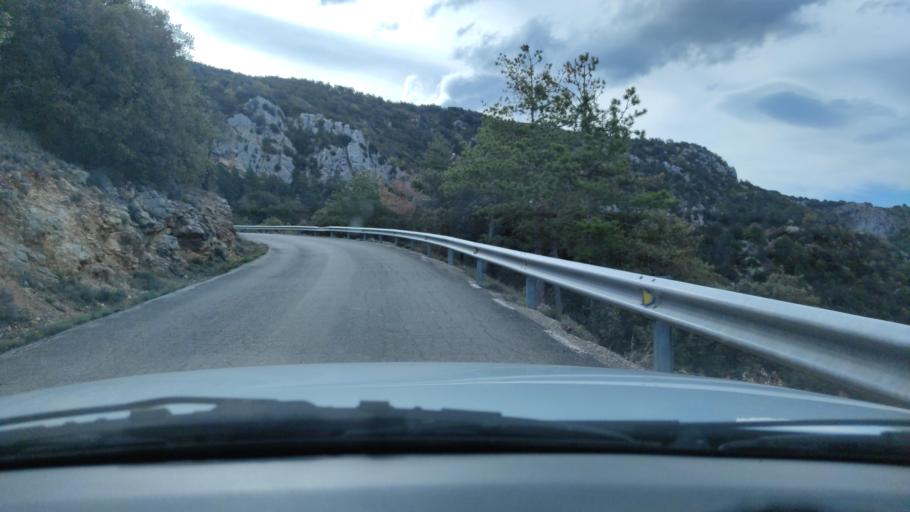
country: ES
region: Catalonia
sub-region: Provincia de Lleida
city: Coll de Nargo
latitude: 42.2487
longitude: 1.3644
